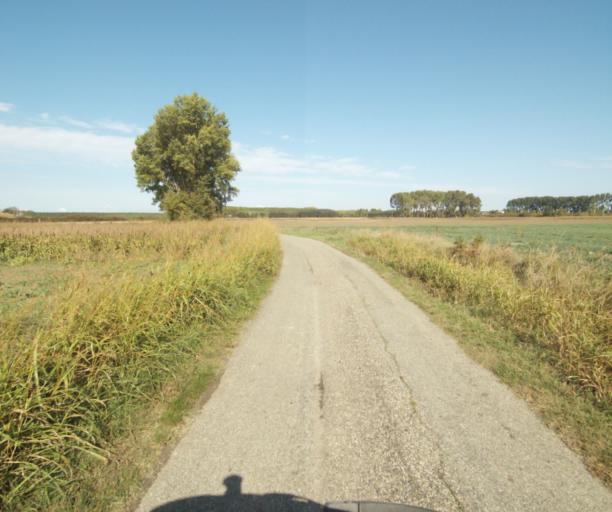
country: FR
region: Midi-Pyrenees
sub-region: Departement du Tarn-et-Garonne
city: Finhan
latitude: 43.8941
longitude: 1.2211
